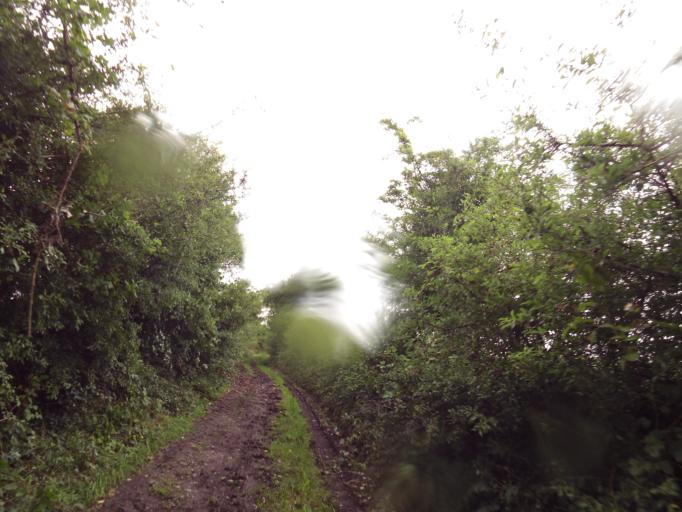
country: IE
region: Connaught
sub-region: County Galway
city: Athenry
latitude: 53.2854
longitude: -8.7066
